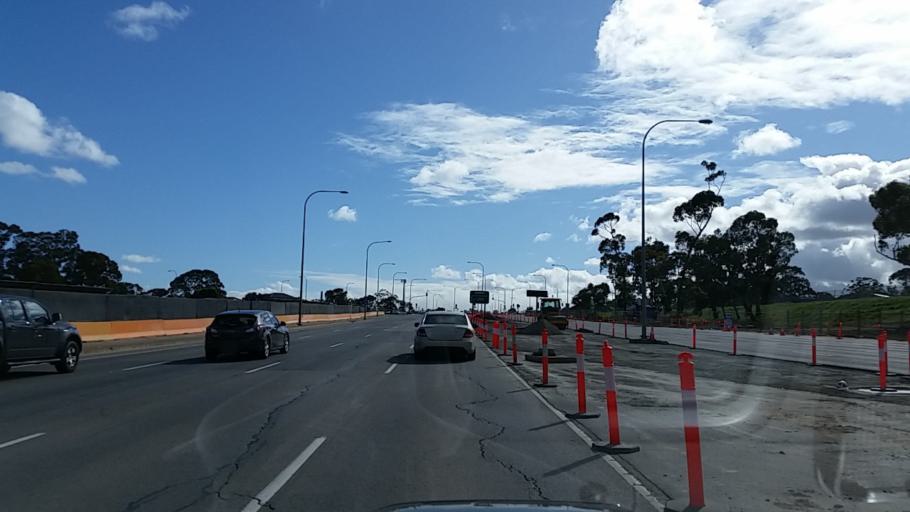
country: AU
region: South Australia
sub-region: Marion
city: Marion
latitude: -35.0186
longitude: 138.5675
